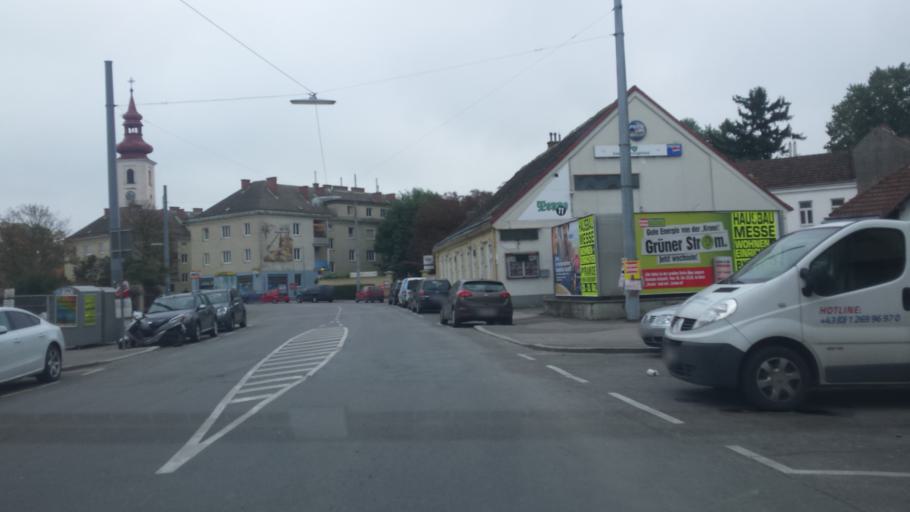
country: AT
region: Lower Austria
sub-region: Politischer Bezirk Wien-Umgebung
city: Schwechat
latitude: 48.1592
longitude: 16.4718
